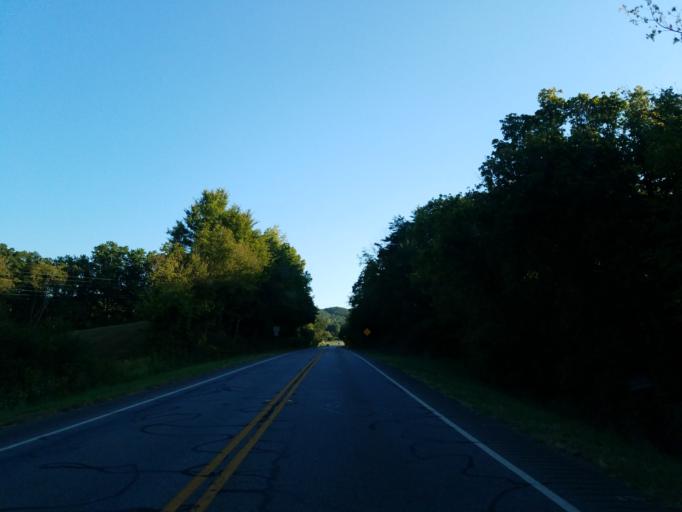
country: US
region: Georgia
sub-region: Bartow County
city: Rydal
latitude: 34.4216
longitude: -84.6982
